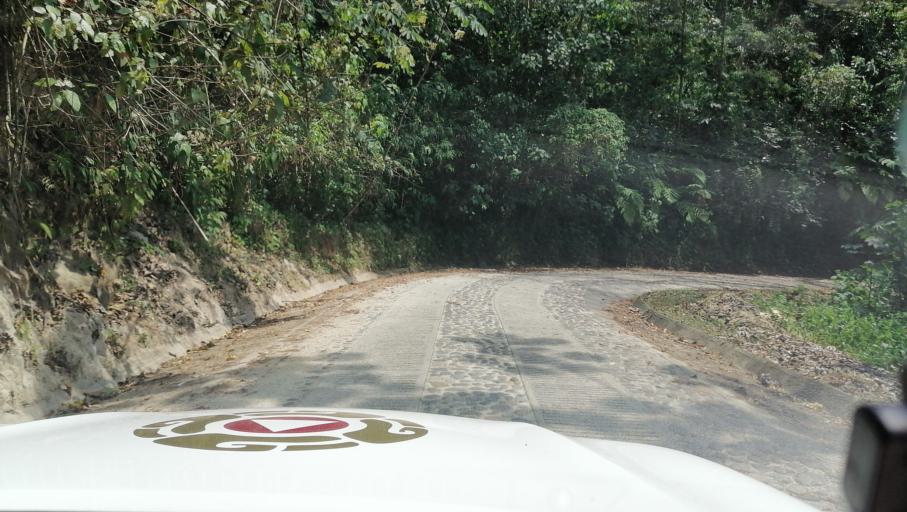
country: MX
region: Chiapas
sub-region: Tapachula
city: Canton Villaflor
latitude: 15.1351
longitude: -92.2920
